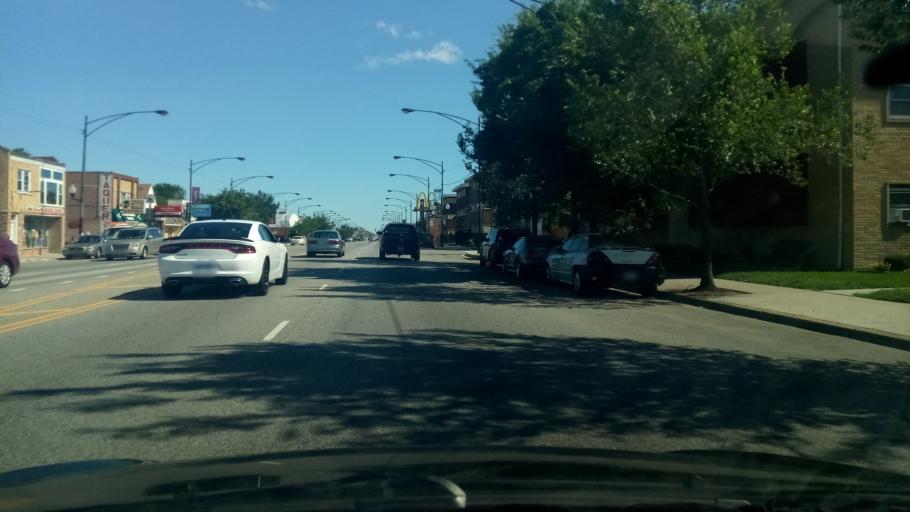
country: US
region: Illinois
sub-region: Cook County
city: Hometown
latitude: 41.7681
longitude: -87.7224
